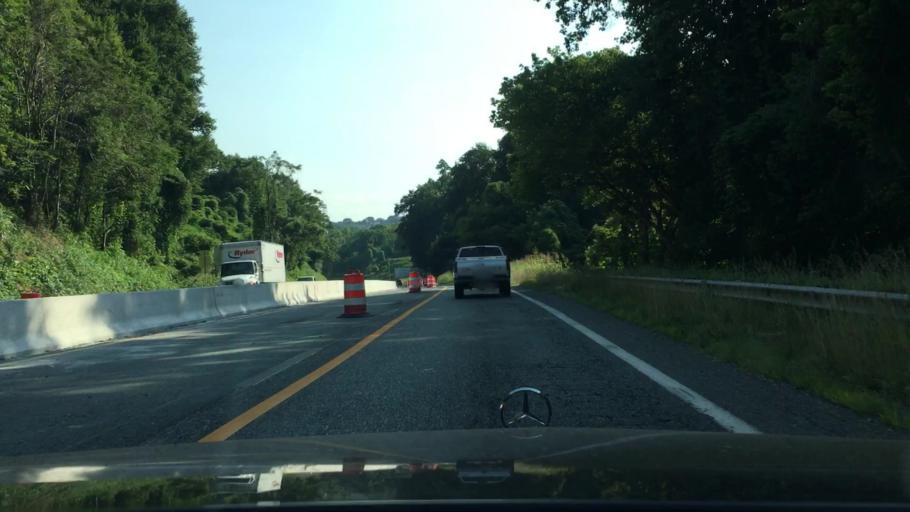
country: US
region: Virginia
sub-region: City of Lynchburg
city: Lynchburg
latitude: 37.4166
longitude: -79.1282
